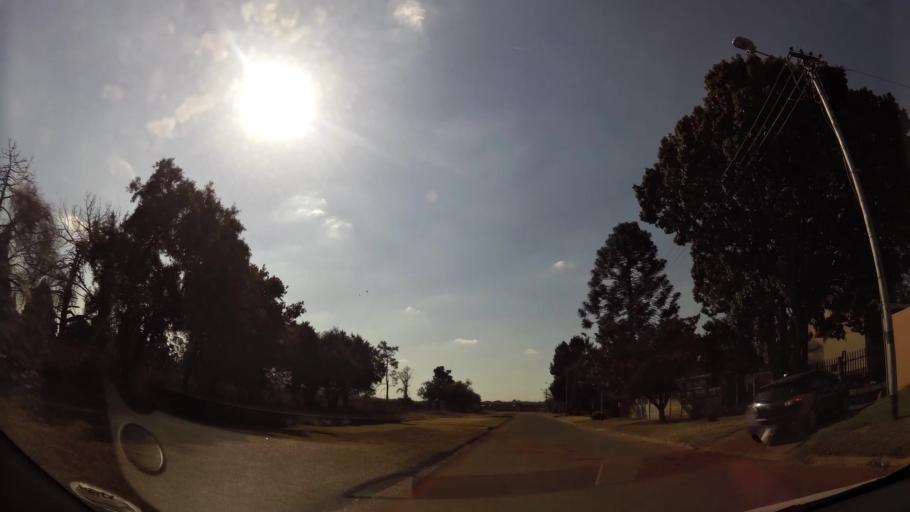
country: ZA
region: Gauteng
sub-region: West Rand District Municipality
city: Randfontein
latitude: -26.1514
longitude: 27.7014
